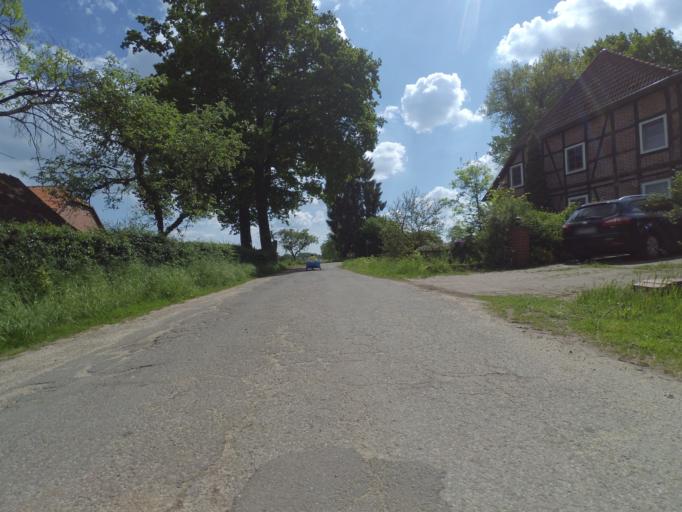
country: DE
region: Lower Saxony
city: Wienhausen
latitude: 52.5796
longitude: 10.2295
